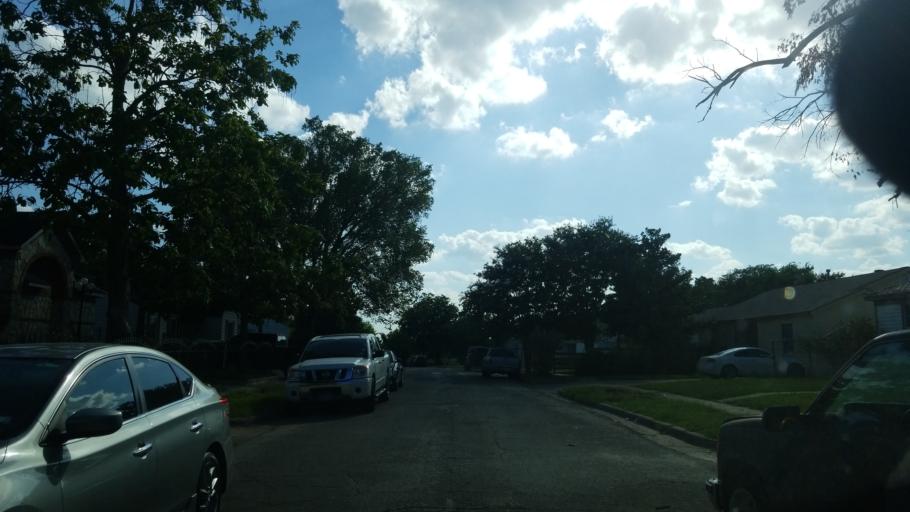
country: US
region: Texas
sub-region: Dallas County
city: Balch Springs
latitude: 32.7655
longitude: -96.7100
